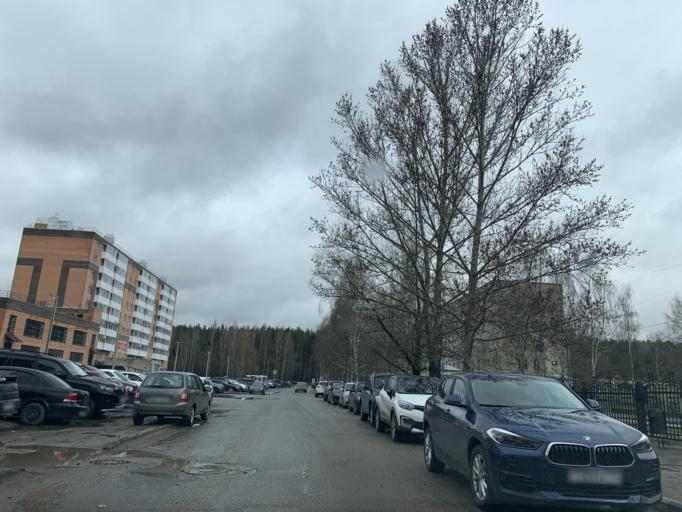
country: RU
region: Jaroslavl
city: Yaroslavl
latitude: 57.6556
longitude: 39.9682
